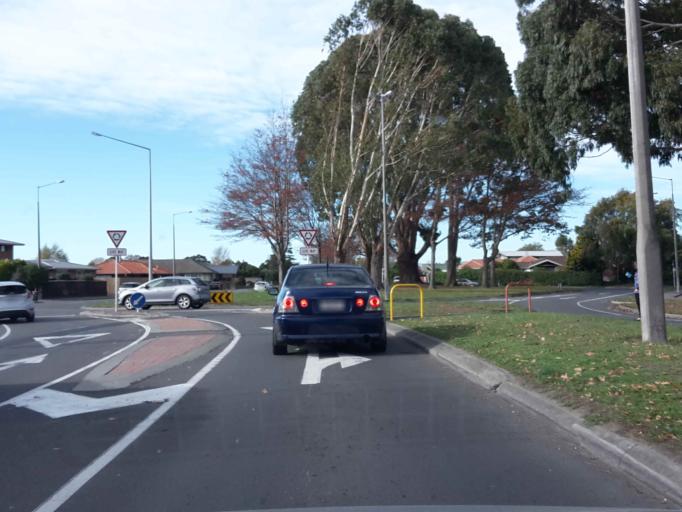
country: NZ
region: Canterbury
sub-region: Christchurch City
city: Christchurch
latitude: -43.4878
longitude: 172.5877
